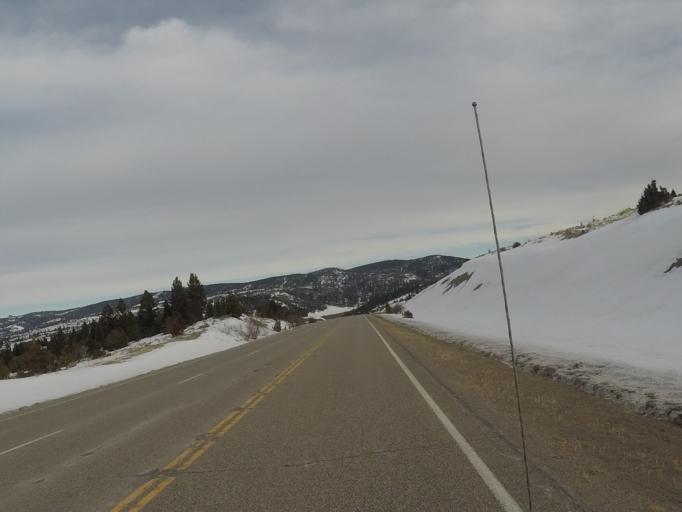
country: US
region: Montana
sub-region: Meagher County
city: White Sulphur Springs
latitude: 46.6579
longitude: -110.8731
